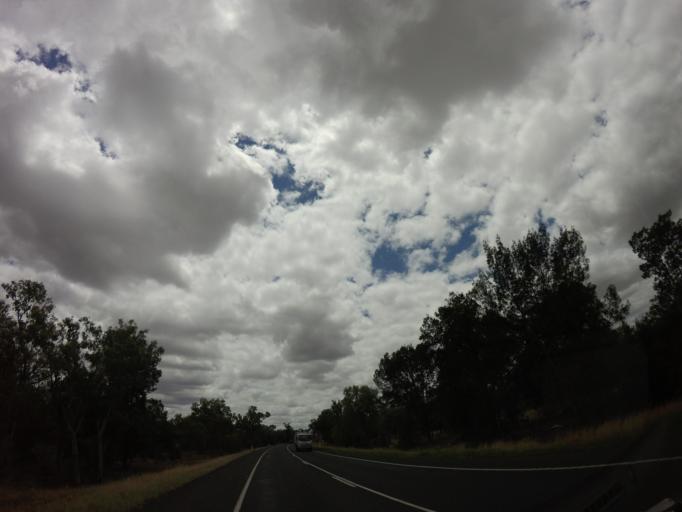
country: AU
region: Queensland
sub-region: Goondiwindi
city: Goondiwindi
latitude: -28.4019
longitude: 150.3076
